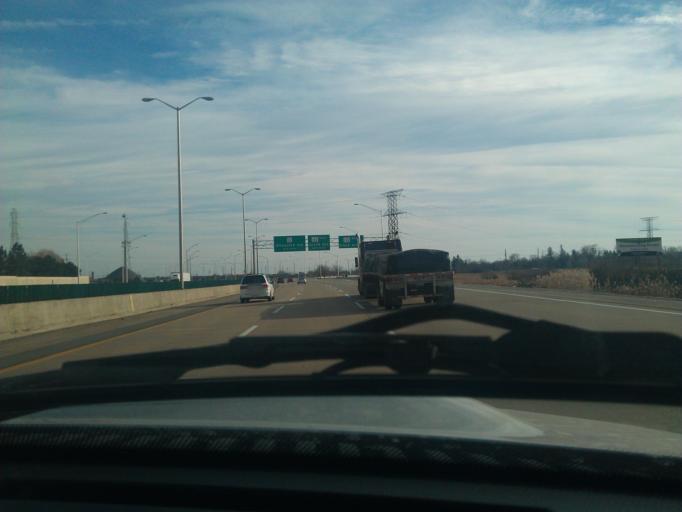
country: US
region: Illinois
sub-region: Lake County
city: Grandwood Park
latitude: 42.3885
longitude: -87.9494
